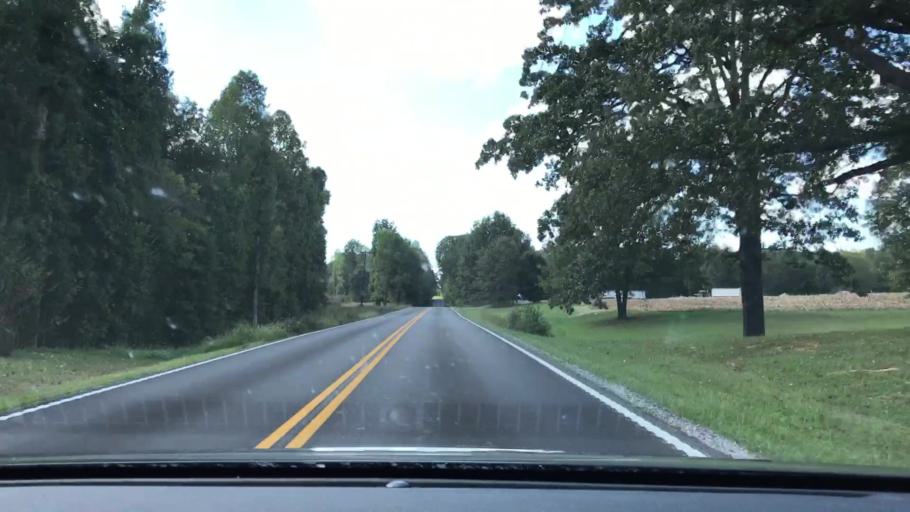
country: US
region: Kentucky
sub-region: McCracken County
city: Reidland
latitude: 36.8754
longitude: -88.5660
